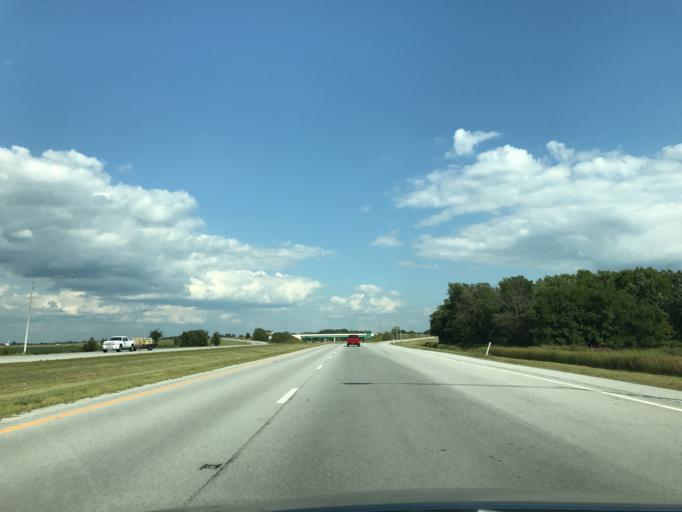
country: US
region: Ohio
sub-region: Allen County
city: Delphos
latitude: 40.8733
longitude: -84.3566
